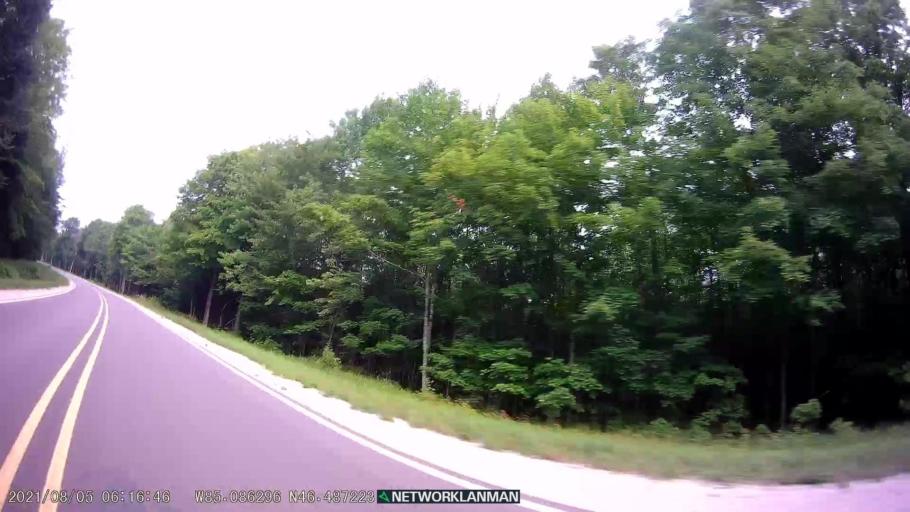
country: US
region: Michigan
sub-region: Luce County
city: Newberry
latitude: 46.4868
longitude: -85.0888
